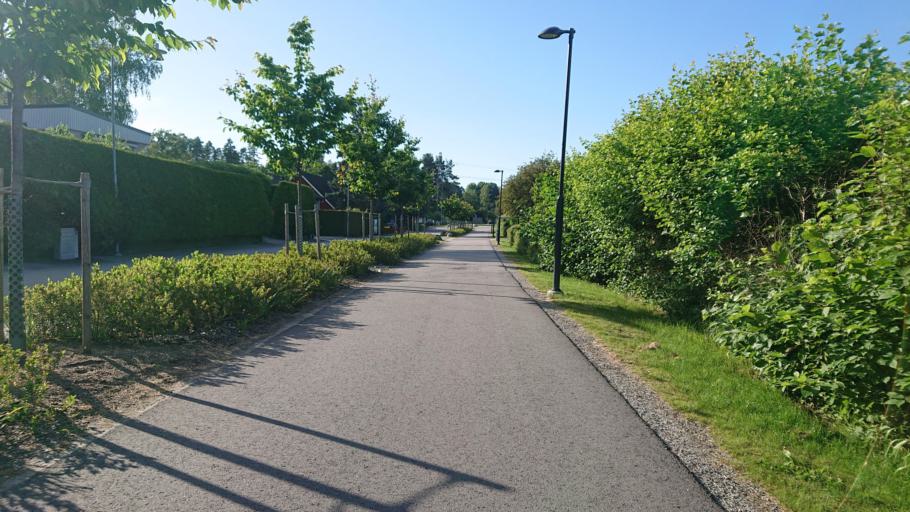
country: SE
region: Stockholm
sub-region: Osterakers Kommun
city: Akersberga
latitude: 59.4913
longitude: 18.2899
